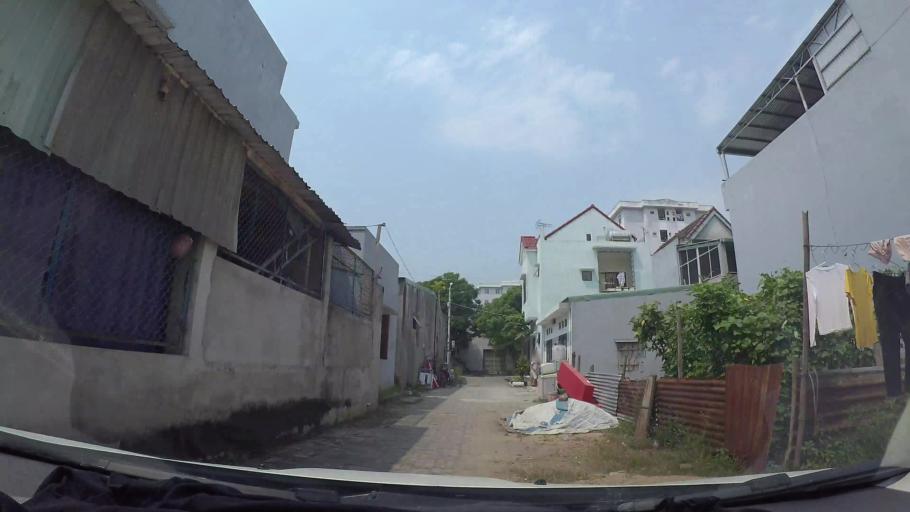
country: VN
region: Da Nang
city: Cam Le
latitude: 16.0011
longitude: 108.2058
